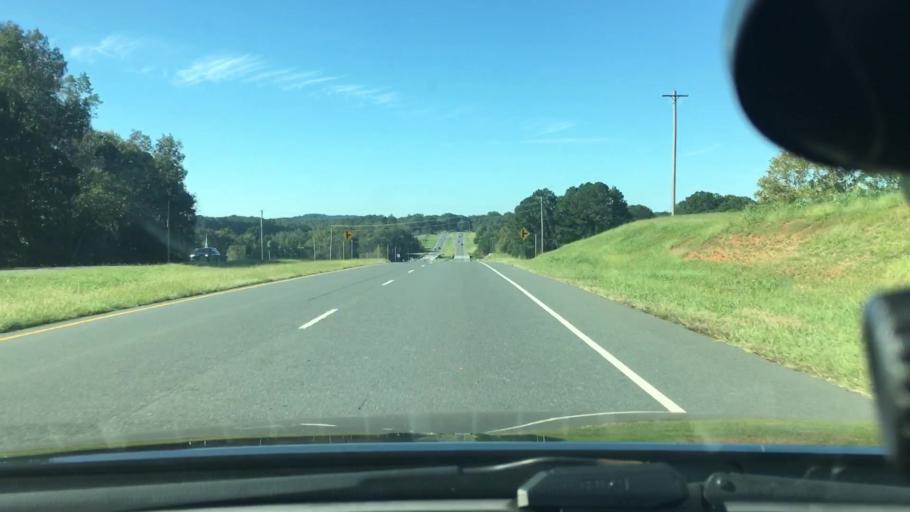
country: US
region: North Carolina
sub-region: Stanly County
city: Oakboro
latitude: 35.2844
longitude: -80.2976
